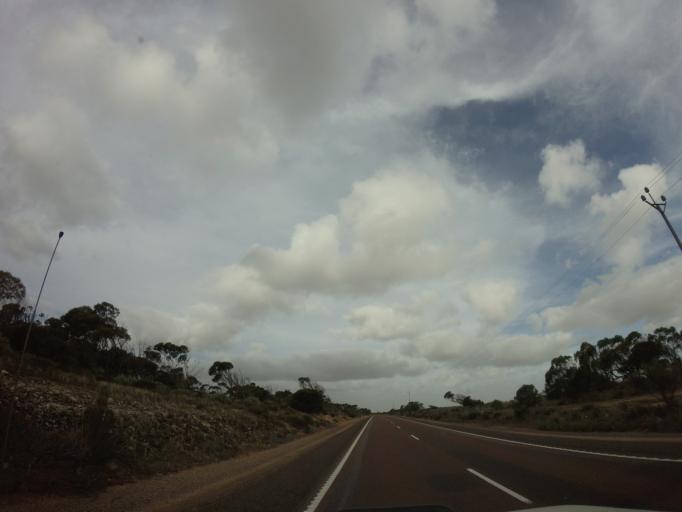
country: AU
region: South Australia
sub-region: Ceduna
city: Ceduna
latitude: -32.0663
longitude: 133.6414
